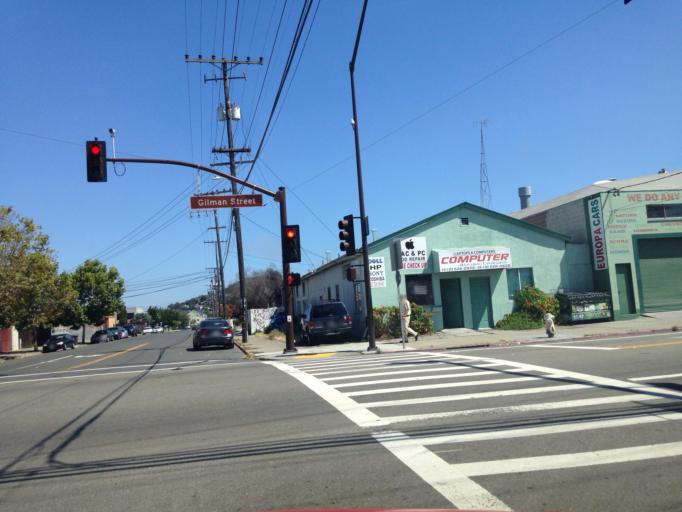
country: US
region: California
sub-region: Alameda County
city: Albany
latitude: 37.8793
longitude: -122.3013
